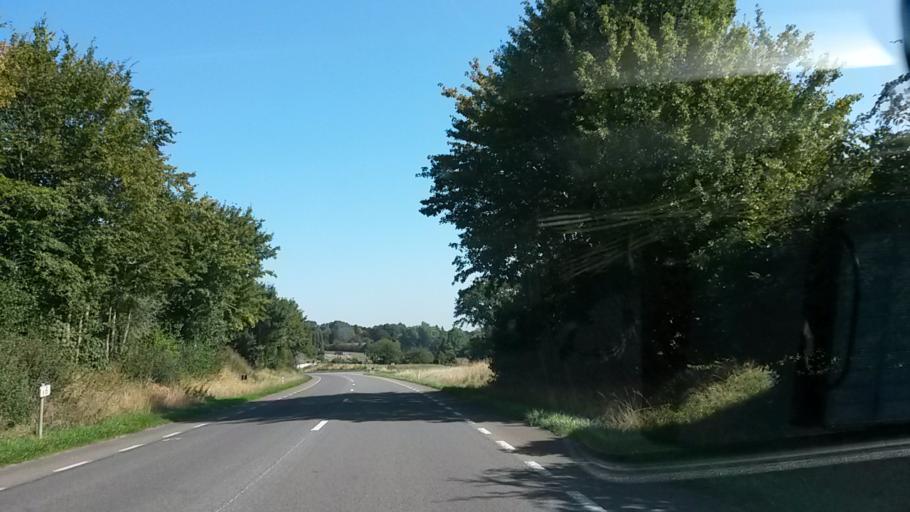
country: BE
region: Wallonia
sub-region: Province du Hainaut
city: Merbes-le-Chateau
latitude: 50.3172
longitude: 4.1476
